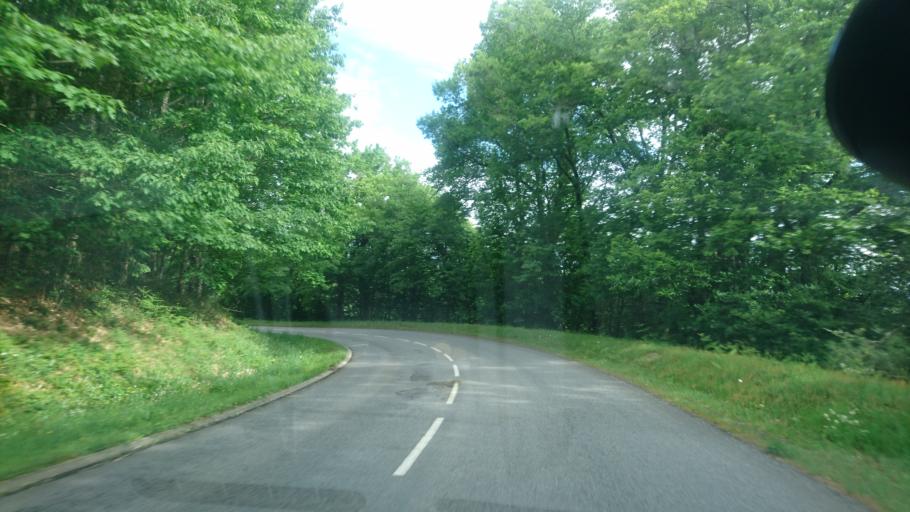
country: FR
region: Limousin
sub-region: Departement de la Haute-Vienne
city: Peyrat-le-Chateau
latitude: 45.7894
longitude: 1.7639
